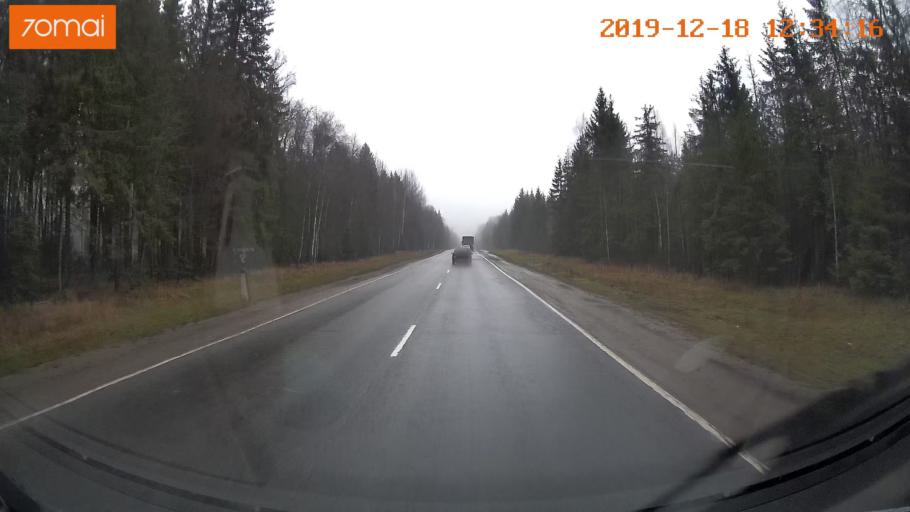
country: RU
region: Moskovskaya
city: Rumyantsevo
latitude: 56.1197
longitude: 36.5701
